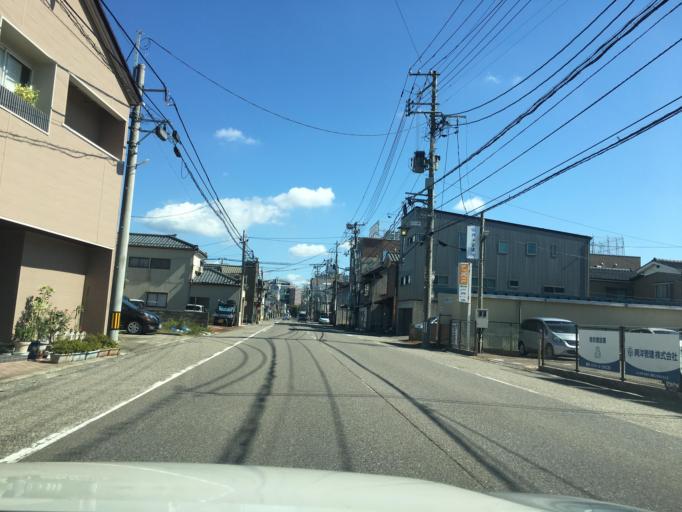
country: JP
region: Niigata
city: Niigata-shi
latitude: 37.9135
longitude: 139.0309
